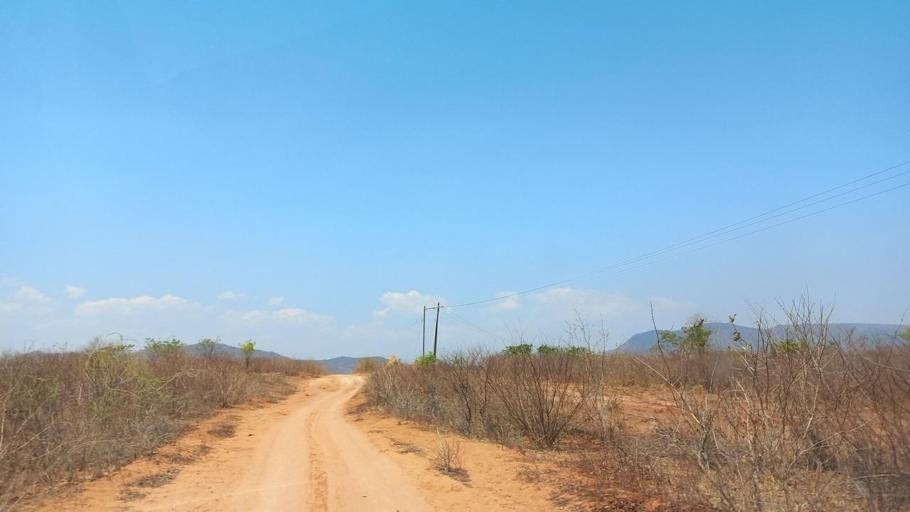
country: ZM
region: Lusaka
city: Luangwa
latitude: -15.5919
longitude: 30.3867
